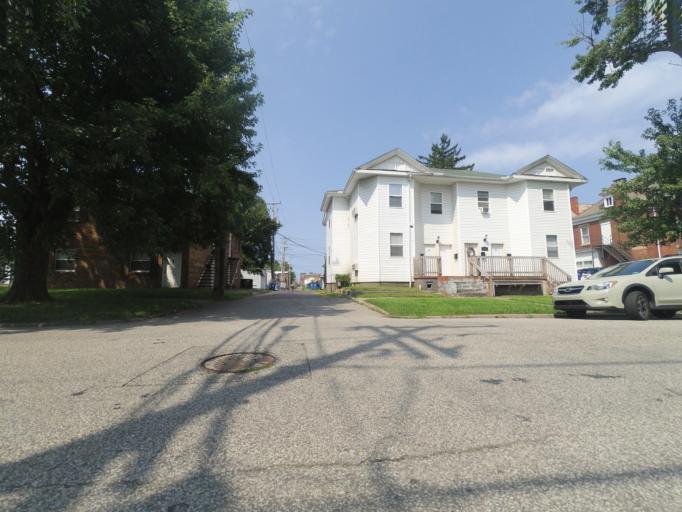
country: US
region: West Virginia
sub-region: Cabell County
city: Huntington
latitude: 38.4192
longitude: -82.4326
